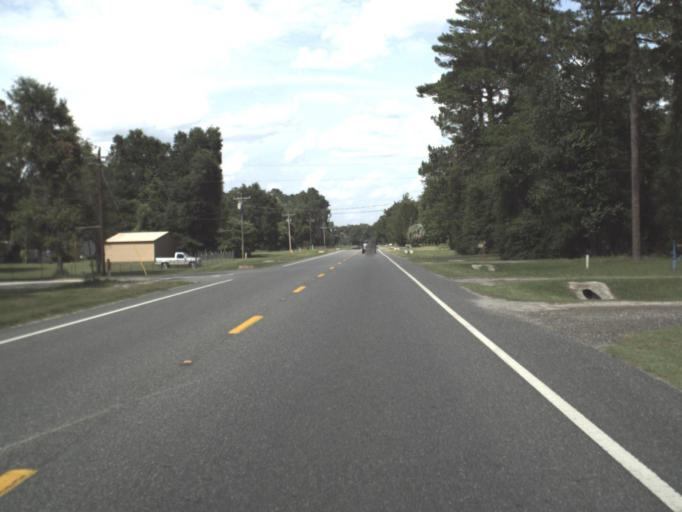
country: US
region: Florida
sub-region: Columbia County
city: Lake City
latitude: 30.0931
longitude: -82.6766
